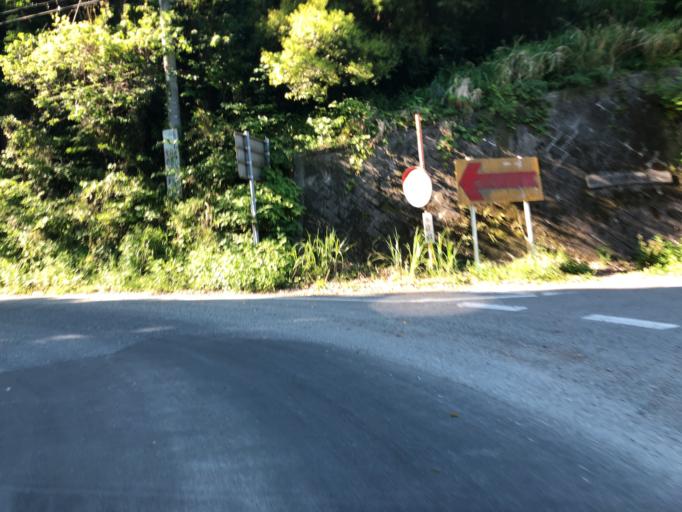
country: JP
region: Ibaraki
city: Kitaibaraki
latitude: 36.8617
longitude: 140.7216
